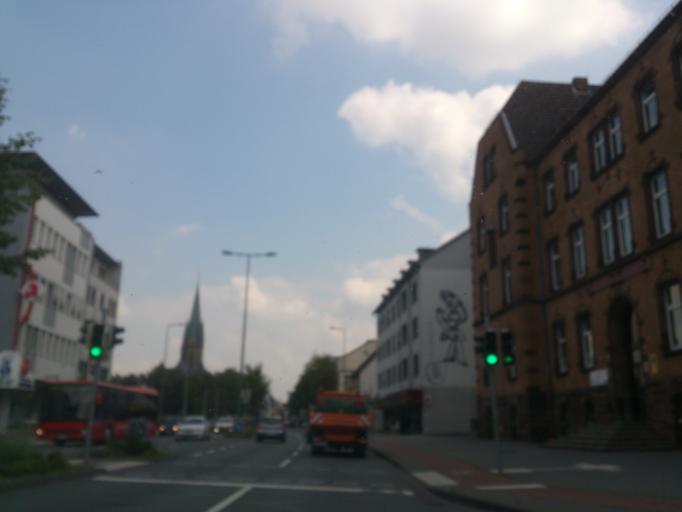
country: DE
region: North Rhine-Westphalia
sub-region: Regierungsbezirk Detmold
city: Paderborn
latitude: 51.7138
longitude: 8.7418
